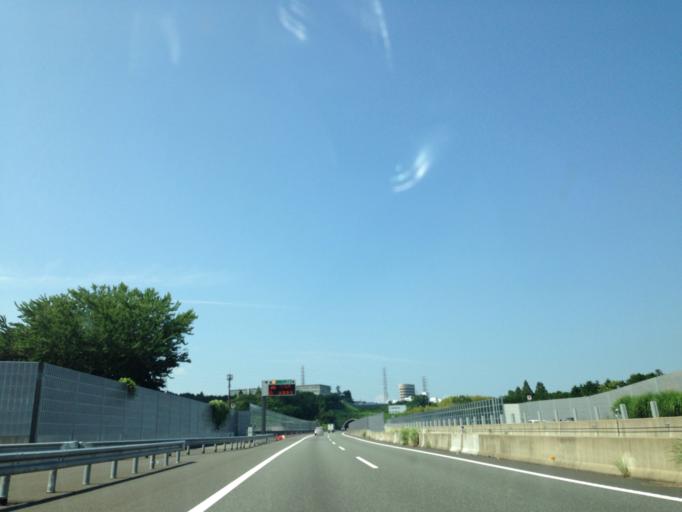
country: JP
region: Shizuoka
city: Gotemba
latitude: 35.2184
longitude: 138.8872
